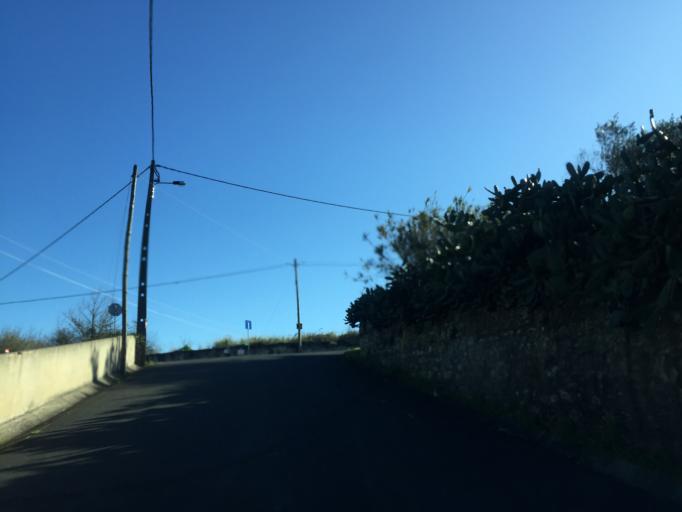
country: PT
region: Lisbon
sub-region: Sintra
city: Pero Pinheiro
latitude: 38.8501
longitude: -9.3173
